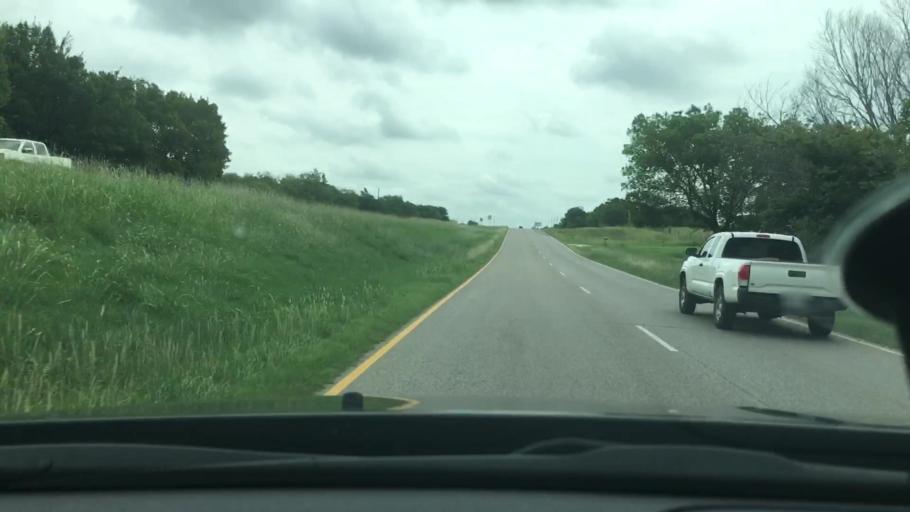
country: US
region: Oklahoma
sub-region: Carter County
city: Wilson
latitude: 34.1729
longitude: -97.4524
